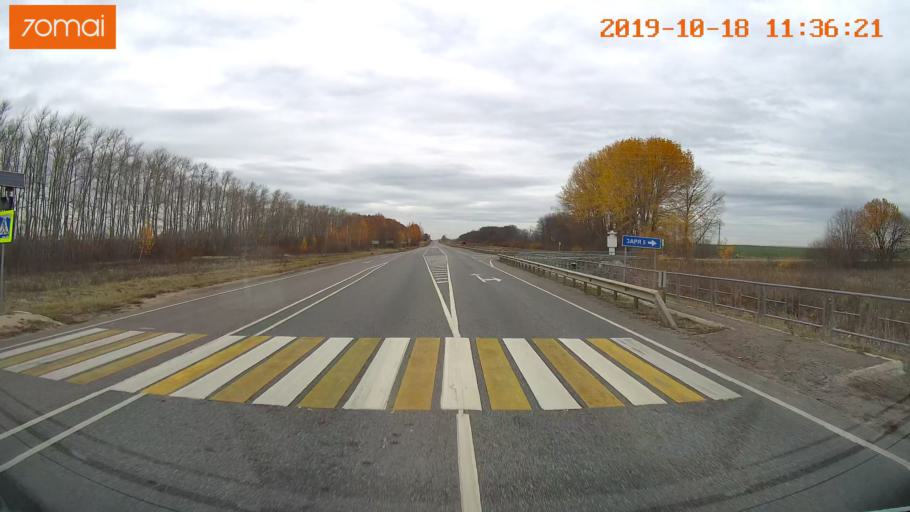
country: RU
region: Rjazan
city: Oktyabr'skiy
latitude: 54.1399
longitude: 38.8046
